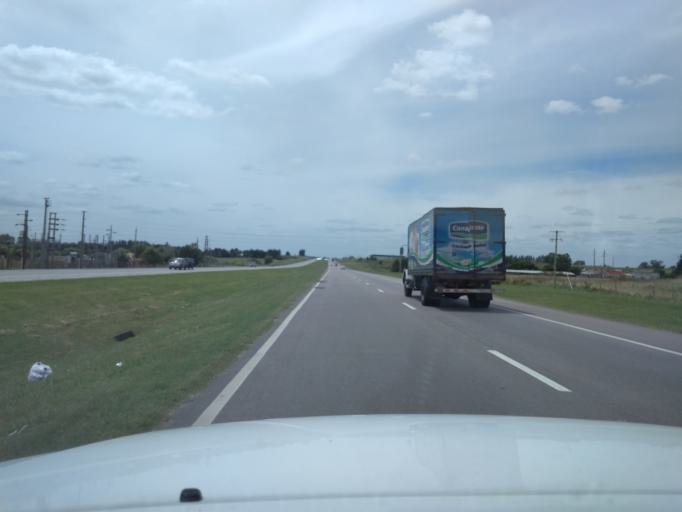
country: UY
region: Canelones
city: Las Piedras
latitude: -34.7139
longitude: -56.2435
